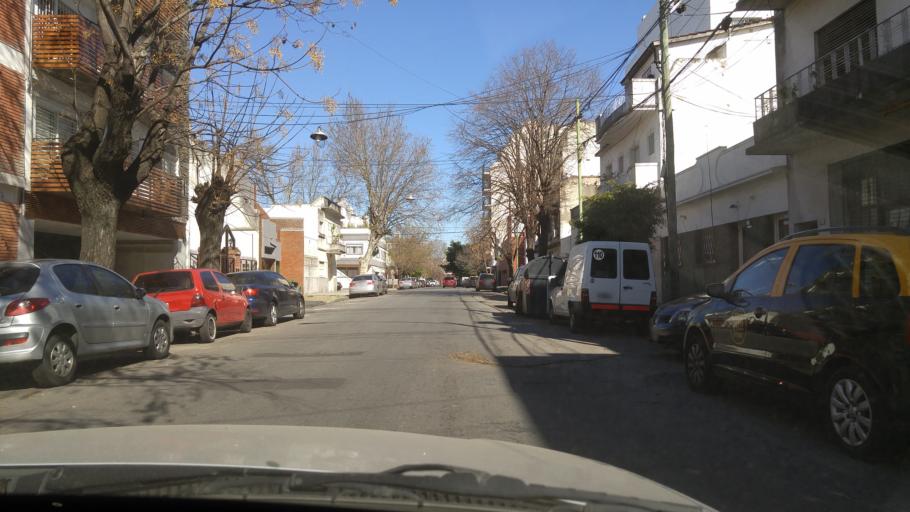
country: AR
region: Buenos Aires F.D.
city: Villa Santa Rita
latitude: -34.6231
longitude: -58.4856
